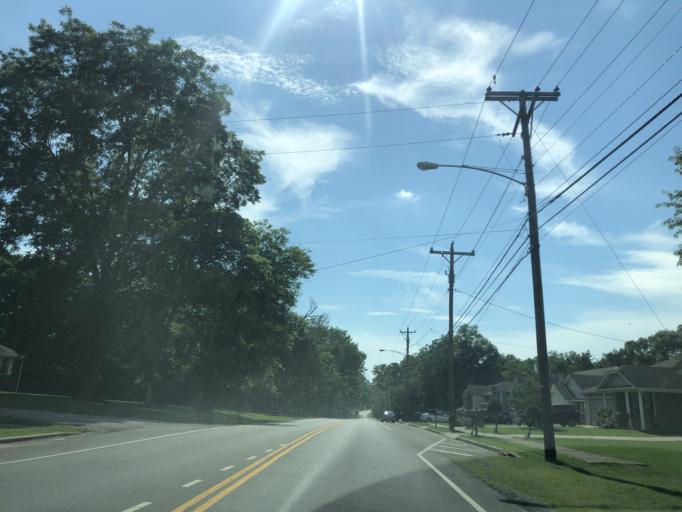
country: US
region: Tennessee
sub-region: Davidson County
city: Nashville
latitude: 36.2315
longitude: -86.7935
